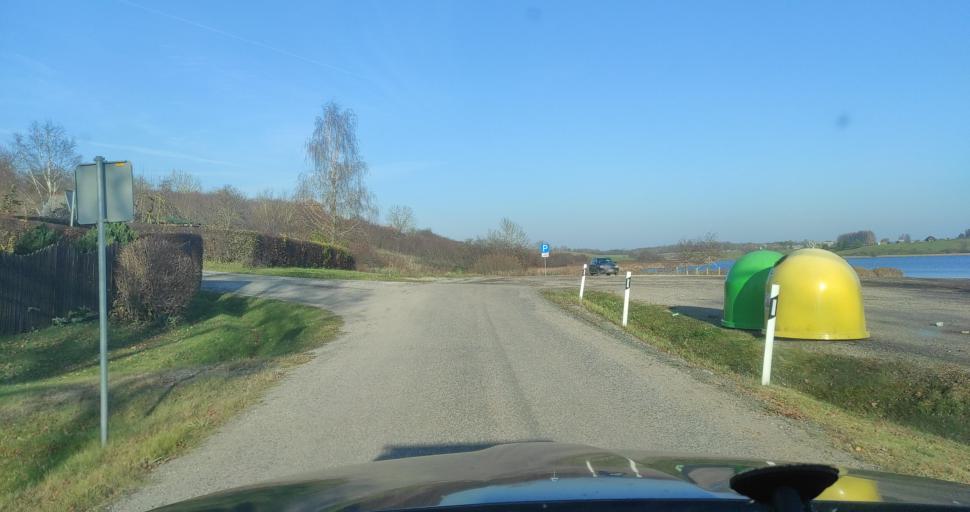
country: LV
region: Saldus Rajons
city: Saldus
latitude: 56.6730
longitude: 22.5043
